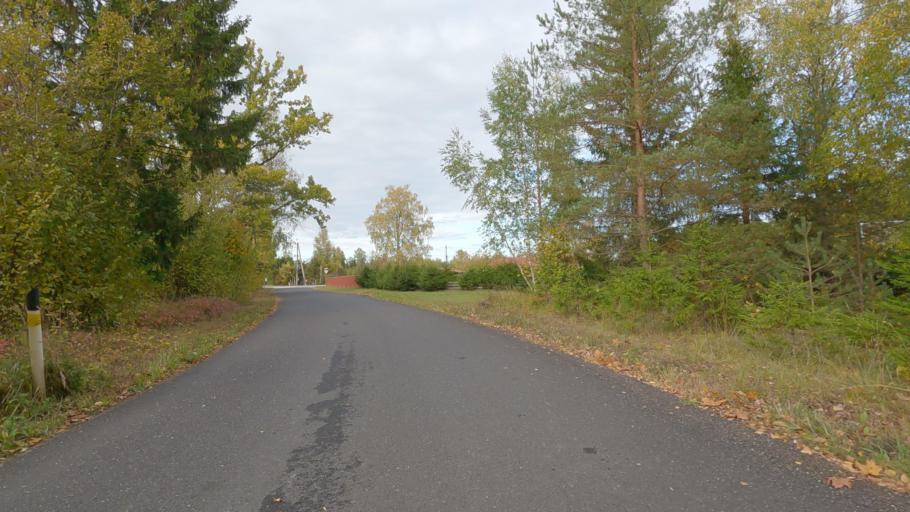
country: EE
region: Raplamaa
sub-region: Rapla vald
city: Rapla
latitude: 58.9785
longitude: 24.7847
